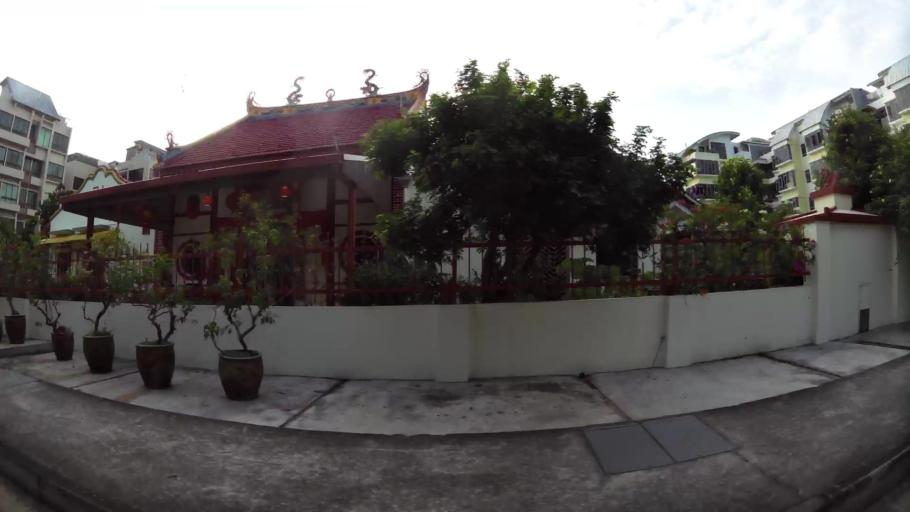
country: SG
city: Singapore
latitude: 1.3124
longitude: 103.9055
